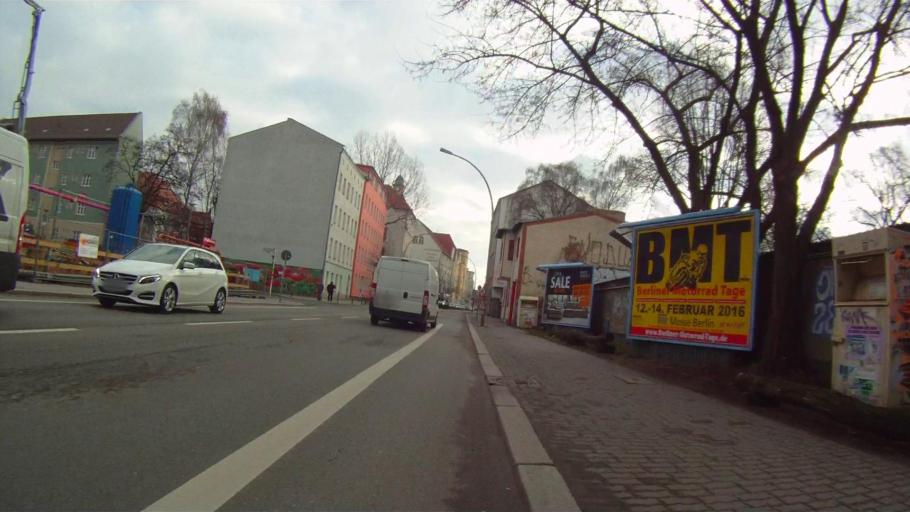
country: DE
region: Berlin
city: Rummelsburg
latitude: 52.5022
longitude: 13.4878
